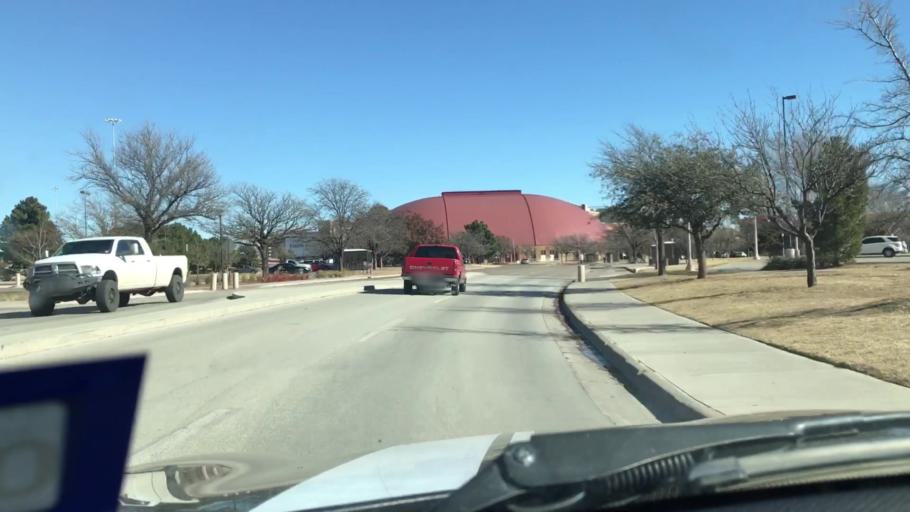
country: US
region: Texas
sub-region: Lubbock County
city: Lubbock
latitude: 33.5885
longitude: -101.8811
